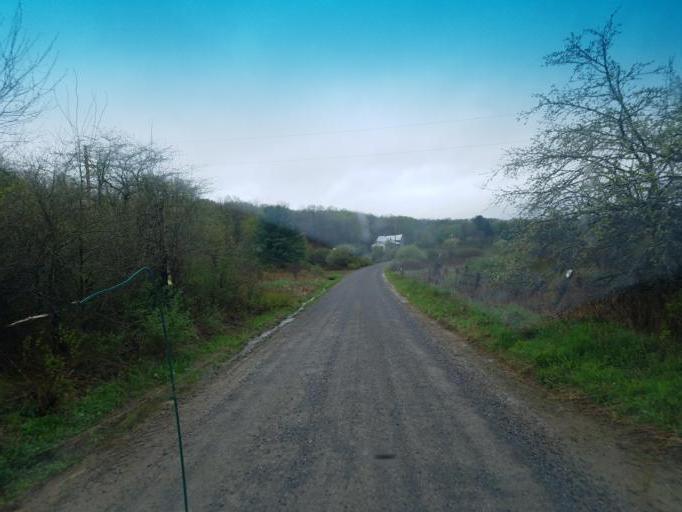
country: US
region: New York
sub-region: Allegany County
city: Andover
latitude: 41.9867
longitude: -77.7440
